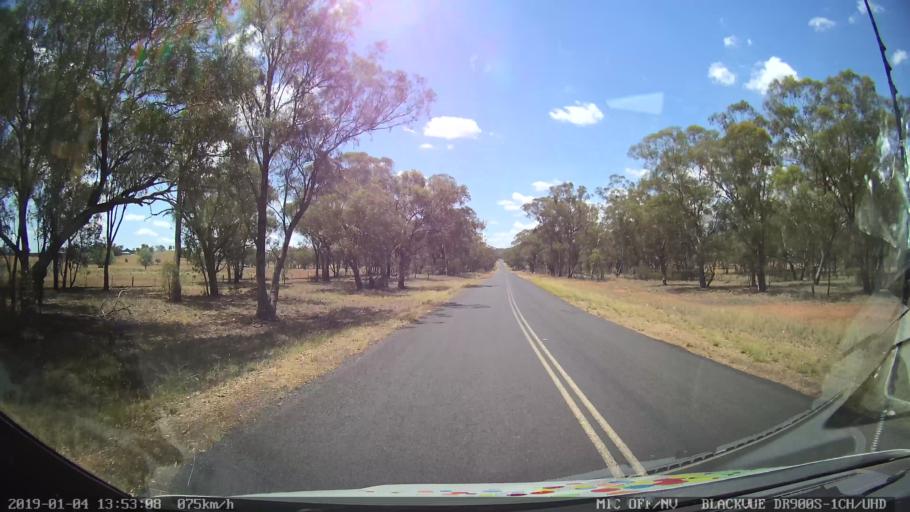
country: AU
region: New South Wales
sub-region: Dubbo Municipality
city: Dubbo
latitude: -32.3863
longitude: 148.5722
